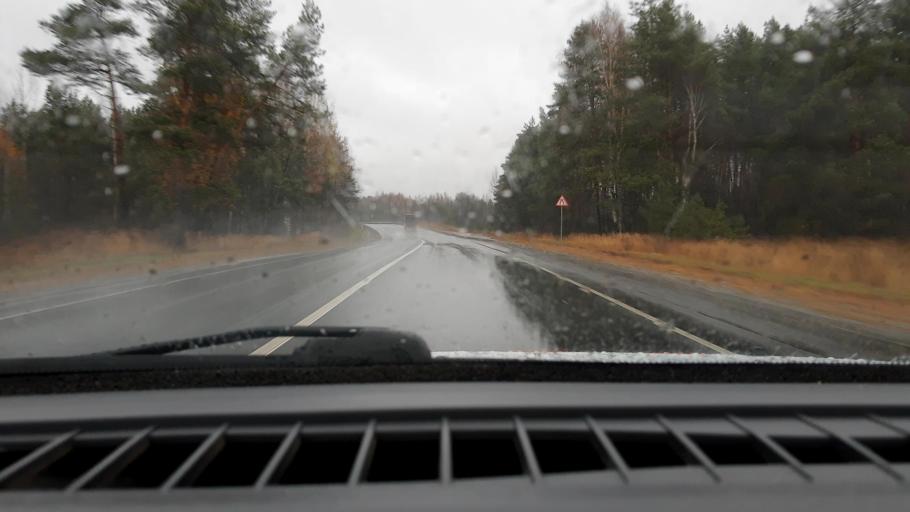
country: RU
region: Nizjnij Novgorod
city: Linda
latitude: 56.6591
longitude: 44.1259
